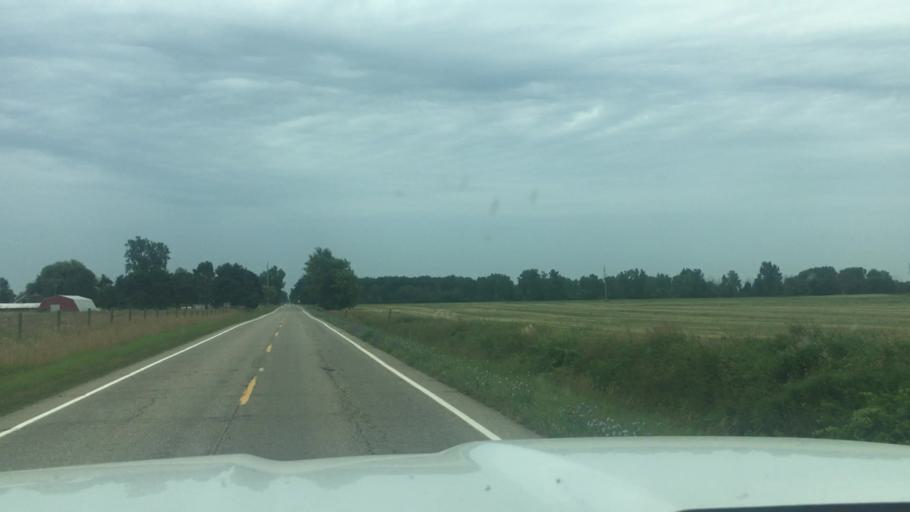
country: US
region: Michigan
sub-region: Clinton County
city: Saint Johns
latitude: 43.0120
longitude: -84.4841
